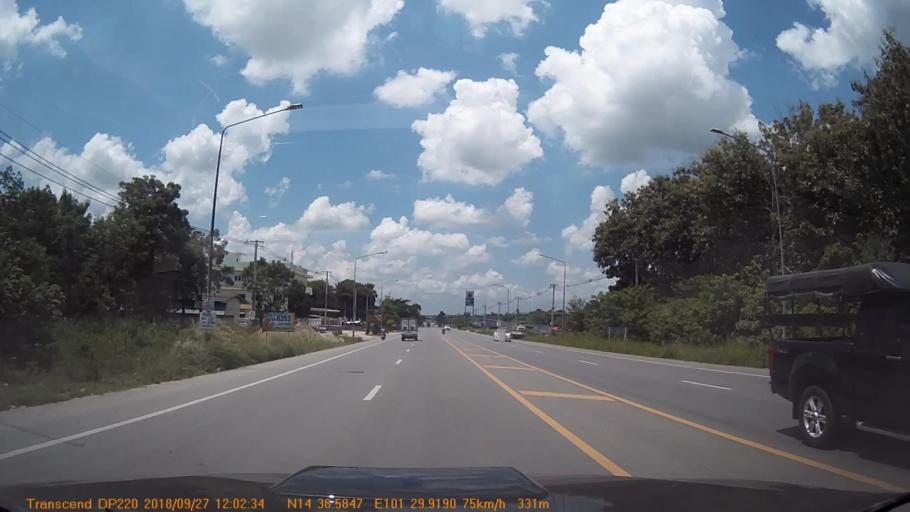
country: TH
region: Nakhon Ratchasima
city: Pak Chong
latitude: 14.6431
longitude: 101.4987
